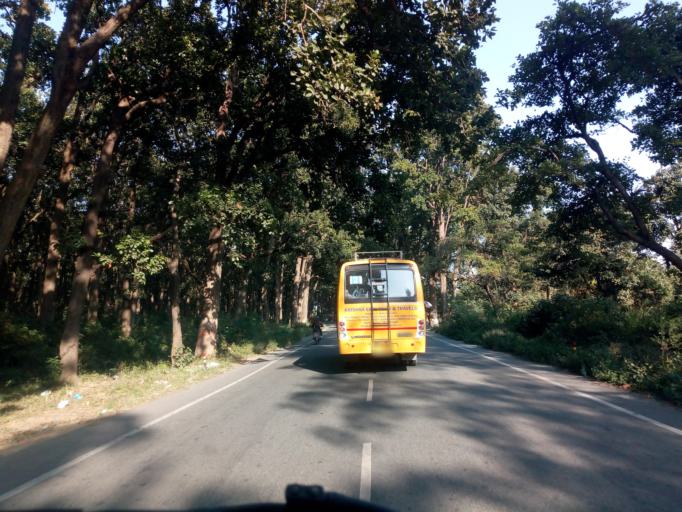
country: IN
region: Uttarakhand
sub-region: Dehradun
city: Dehradun
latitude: 30.3471
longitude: 77.8800
